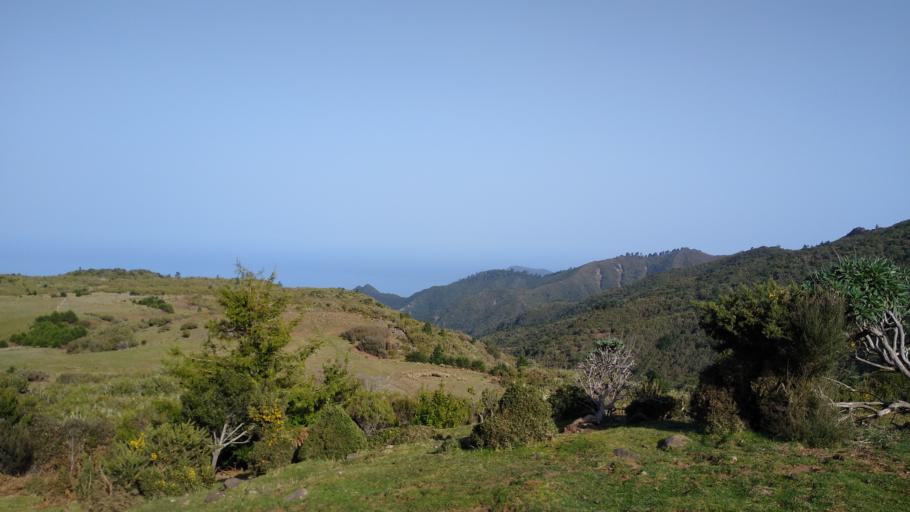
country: PT
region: Madeira
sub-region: Funchal
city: Nossa Senhora do Monte
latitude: 32.7264
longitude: -16.8871
